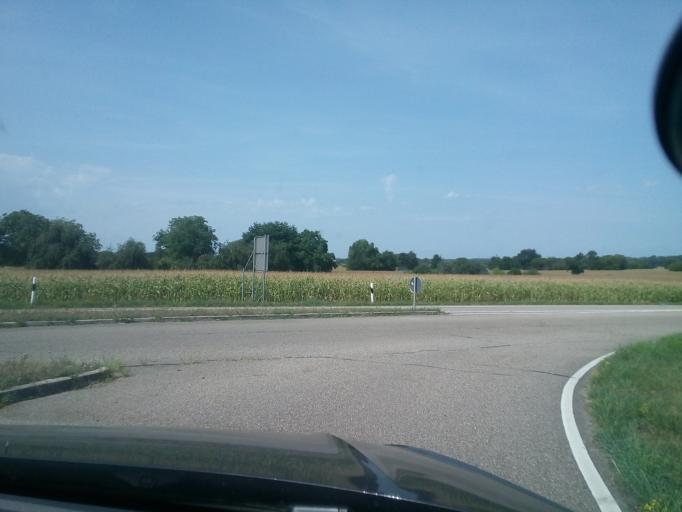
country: DE
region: Baden-Wuerttemberg
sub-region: Karlsruhe Region
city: Kuppenheim
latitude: 48.8148
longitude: 8.2369
